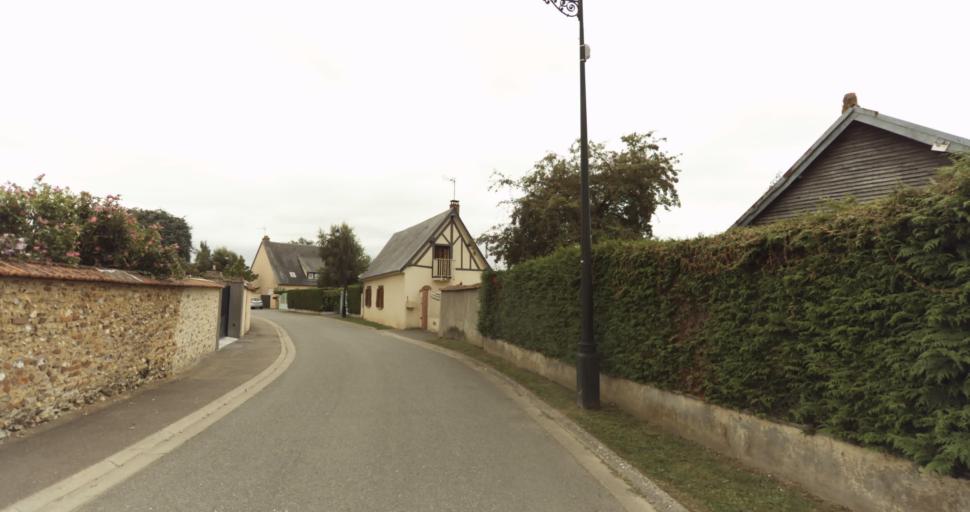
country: FR
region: Haute-Normandie
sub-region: Departement de l'Eure
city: Gravigny
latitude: 49.0369
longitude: 1.2094
